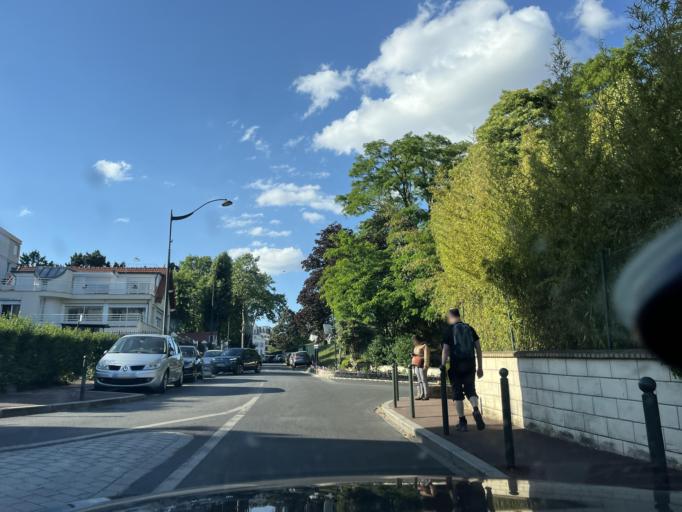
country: FR
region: Ile-de-France
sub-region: Departement des Hauts-de-Seine
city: Le Plessis-Robinson
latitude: 48.7888
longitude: 2.2721
